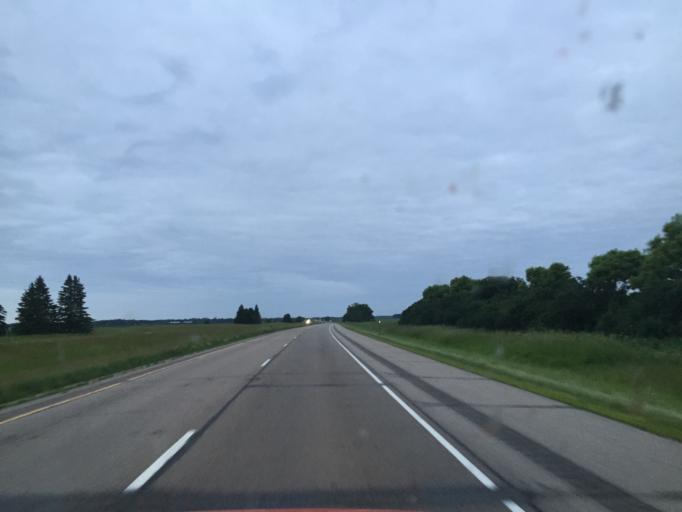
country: US
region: Minnesota
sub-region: Mower County
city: Austin
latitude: 43.6598
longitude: -93.0681
